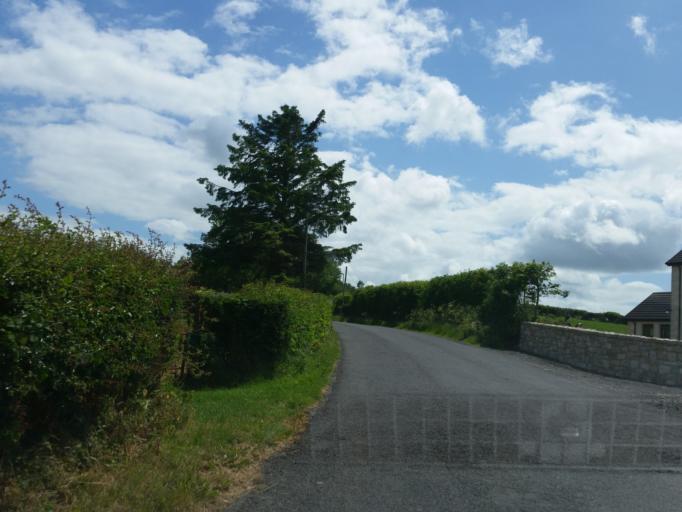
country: GB
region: Northern Ireland
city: Fivemiletown
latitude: 54.3589
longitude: -7.3059
